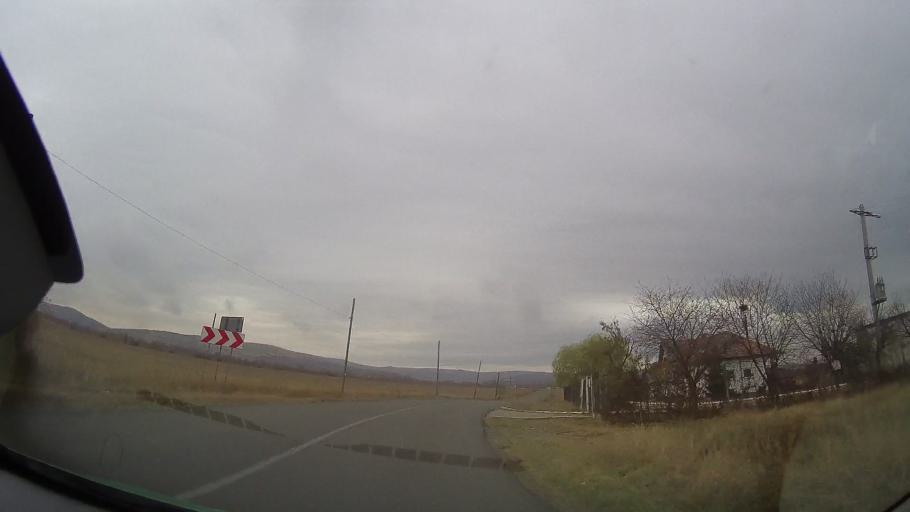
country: RO
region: Prahova
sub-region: Comuna Fantanele
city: Fantanele
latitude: 45.0218
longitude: 26.3805
